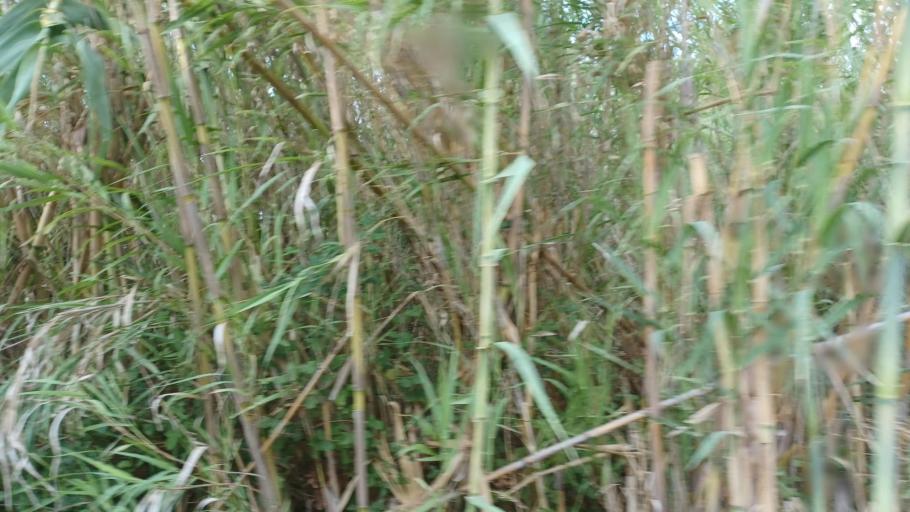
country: CY
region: Pafos
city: Tala
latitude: 34.9115
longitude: 32.4992
